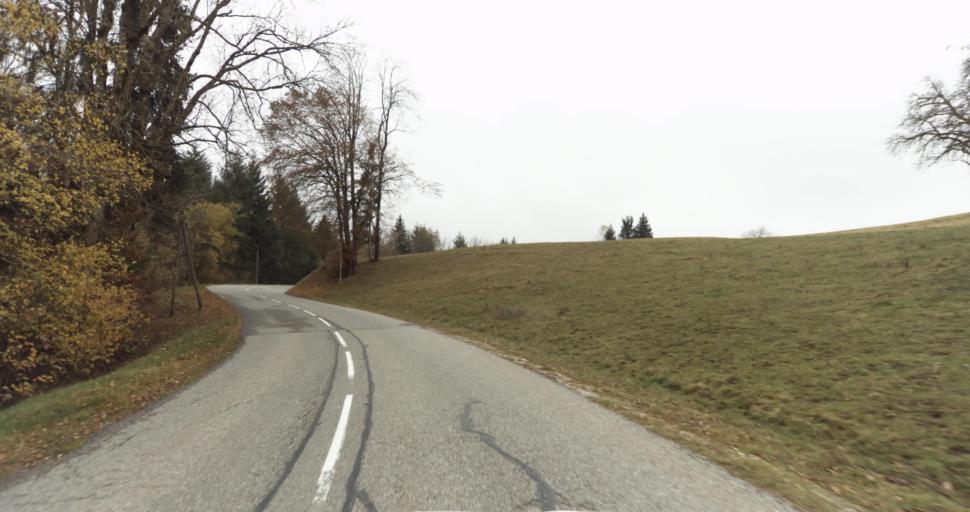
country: FR
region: Rhone-Alpes
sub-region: Departement de la Haute-Savoie
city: Saint-Jorioz
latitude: 45.7744
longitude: 6.1326
